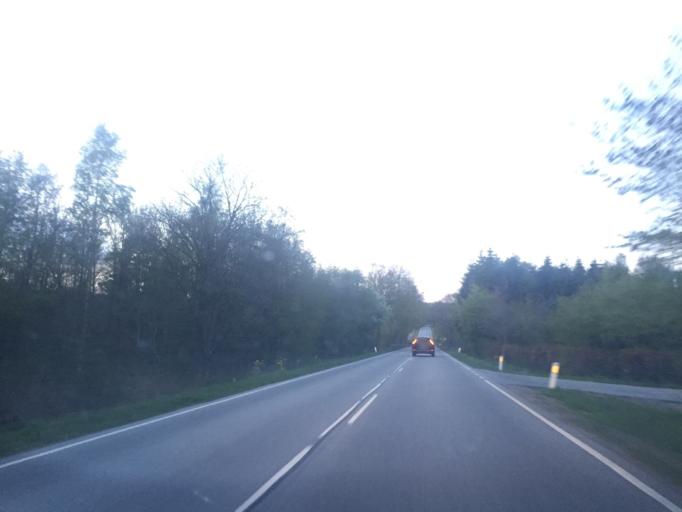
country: DK
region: South Denmark
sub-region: Nyborg Kommune
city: Ullerslev
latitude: 55.2339
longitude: 10.6483
